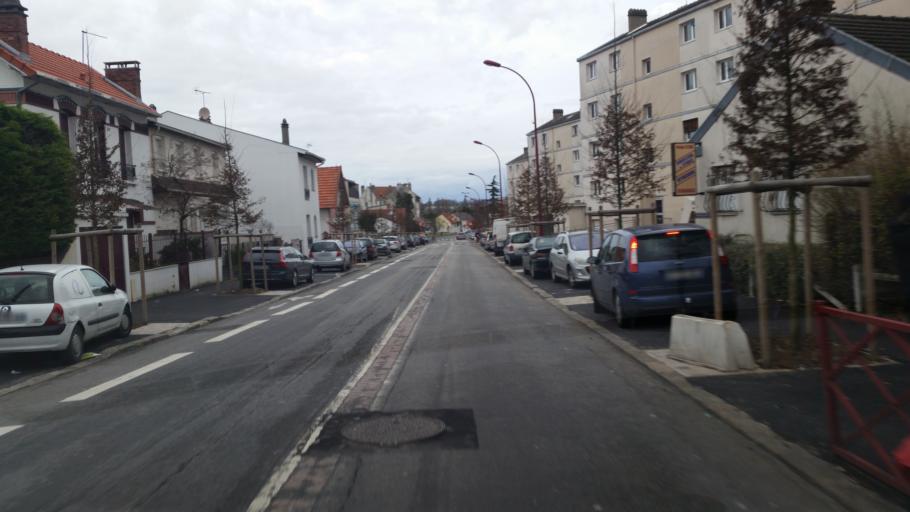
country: FR
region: Ile-de-France
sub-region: Departement du Val-de-Marne
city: Fresnes
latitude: 48.7588
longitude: 2.3200
